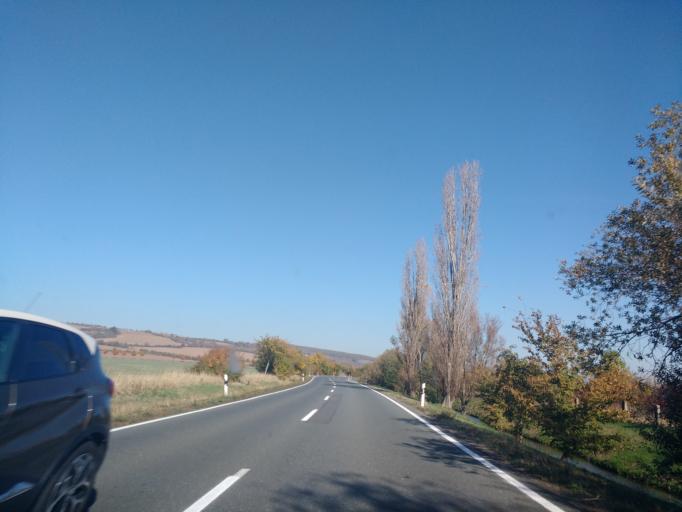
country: DE
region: Saxony-Anhalt
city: Sangerhausen
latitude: 51.4598
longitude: 11.2628
